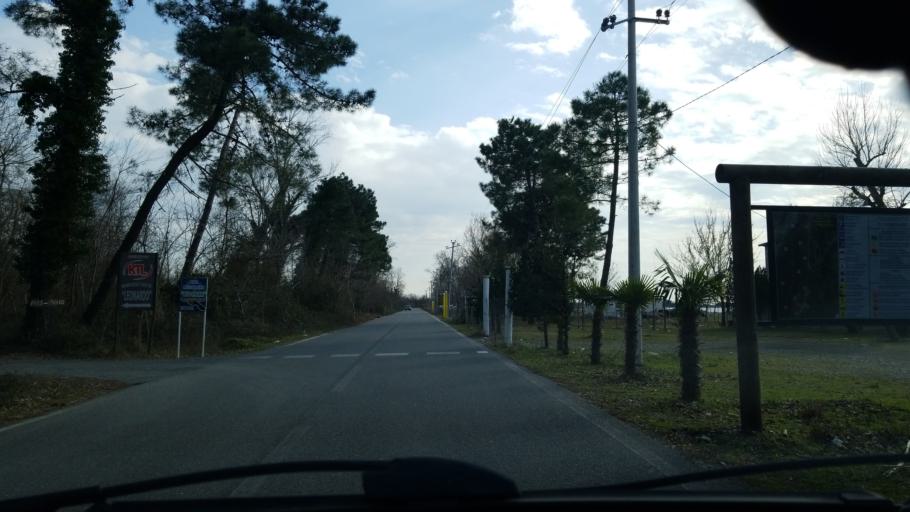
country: AL
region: Lezhe
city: Shengjin
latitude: 41.7790
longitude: 19.6033
